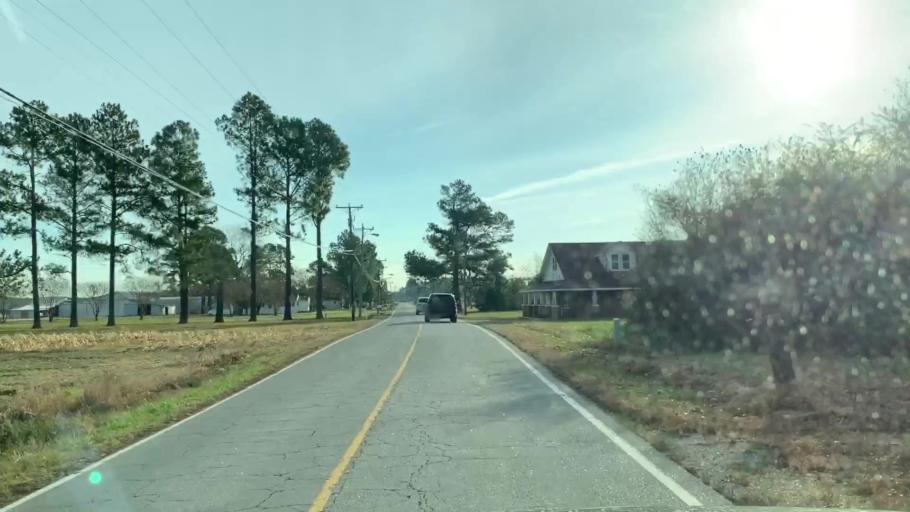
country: US
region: Virginia
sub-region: City of Virginia Beach
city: Virginia Beach
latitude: 36.6919
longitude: -76.0170
